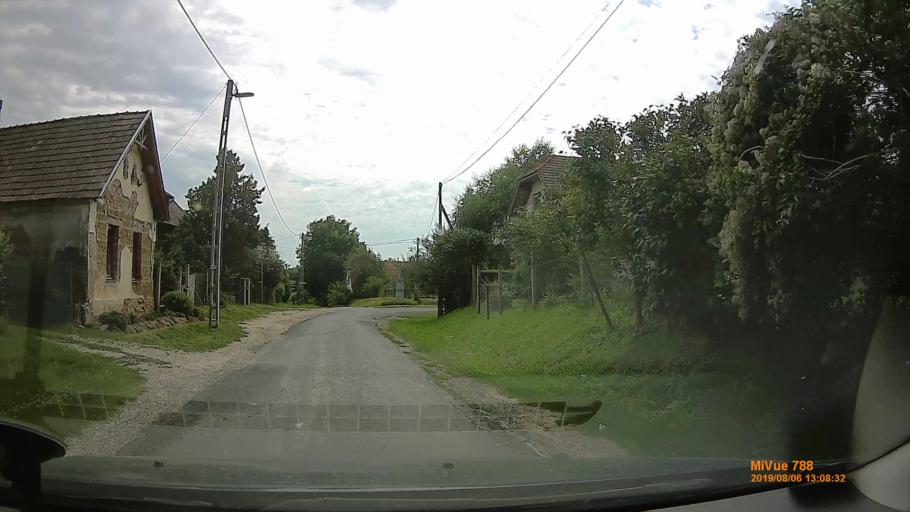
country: HU
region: Zala
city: Pacsa
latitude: 46.6265
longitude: 17.0623
